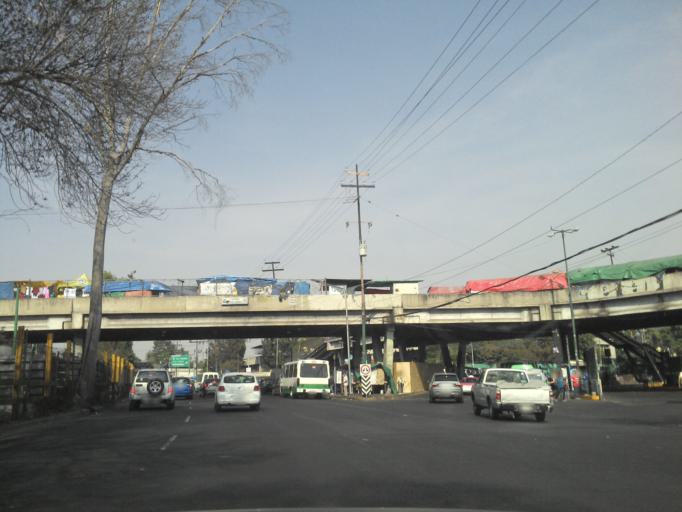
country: MX
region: Mexico City
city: Tlalpan
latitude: 19.3007
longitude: -99.1477
